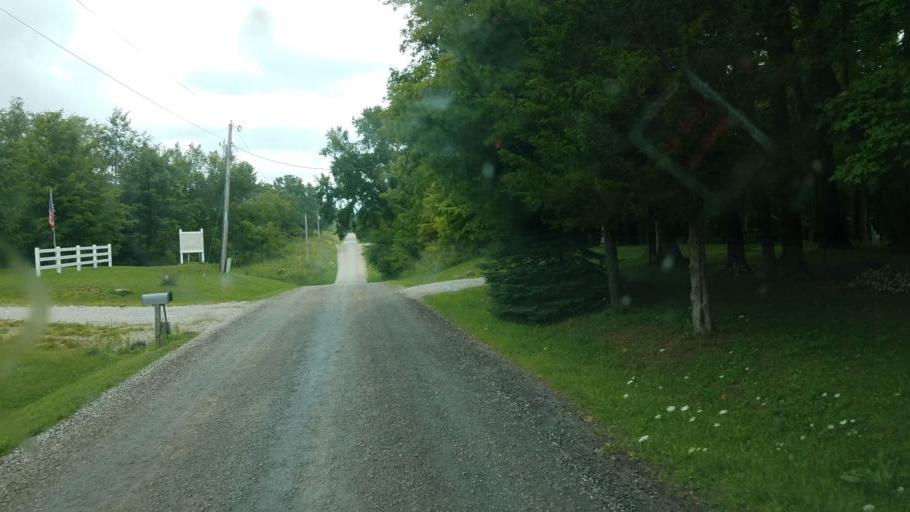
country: US
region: Ohio
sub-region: Morrow County
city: Mount Gilead
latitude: 40.5244
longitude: -82.7015
